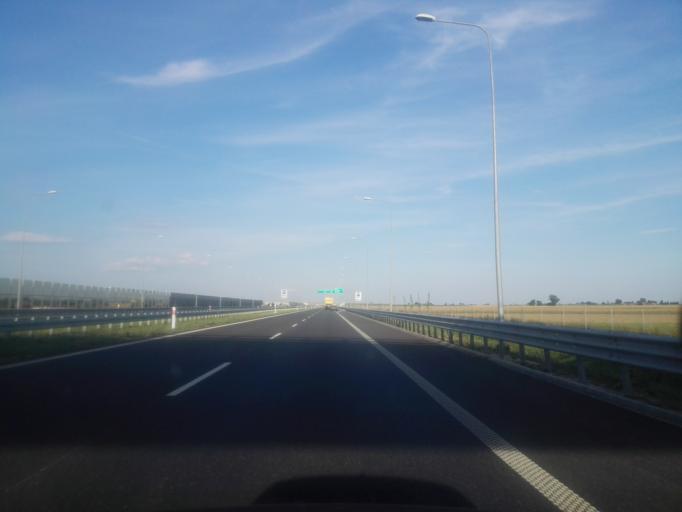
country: PL
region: Lodz Voivodeship
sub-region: Powiat wieruszowski
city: Walichnowy
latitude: 51.3175
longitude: 18.3679
